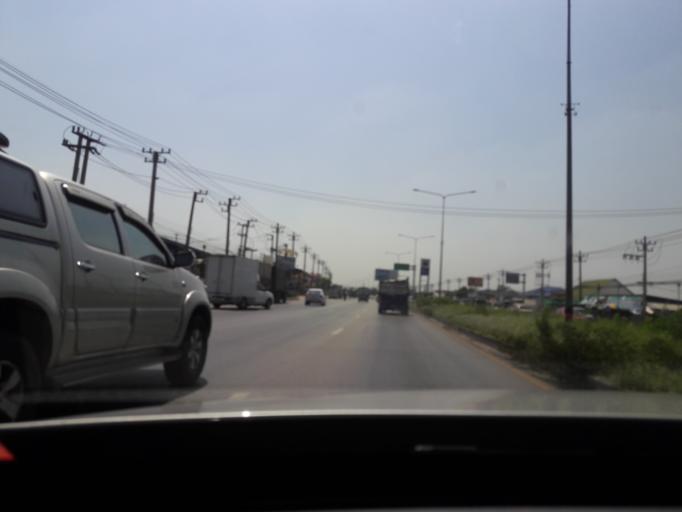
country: TH
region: Bangkok
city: Nong Khaem
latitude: 13.6802
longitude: 100.3209
